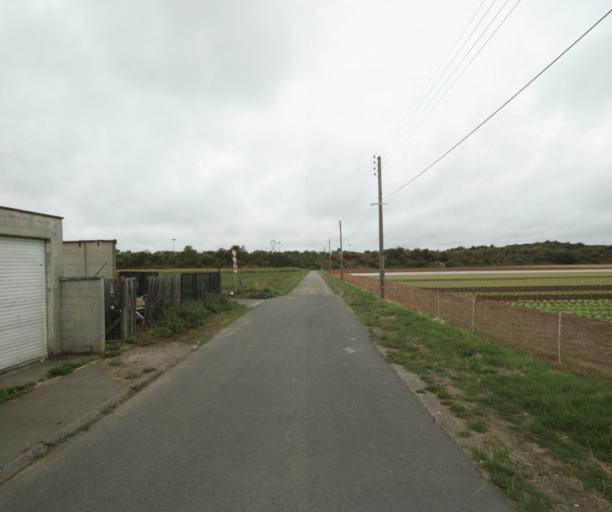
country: FR
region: Nord-Pas-de-Calais
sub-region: Departement du Nord
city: Ronchin
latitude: 50.5956
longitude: 3.1064
